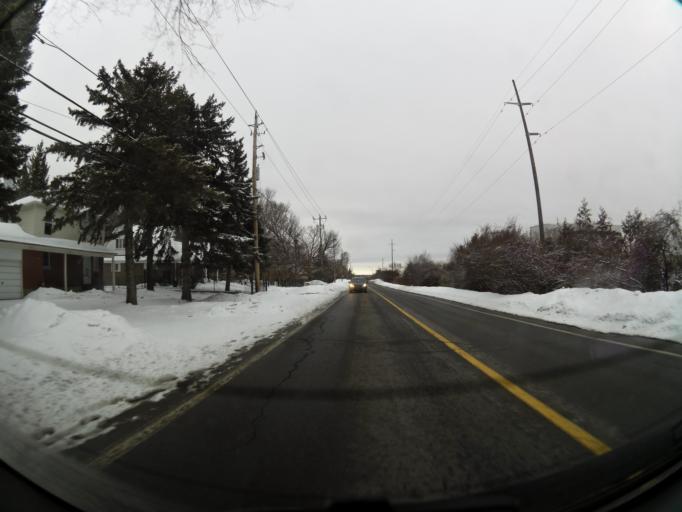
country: CA
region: Quebec
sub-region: Outaouais
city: Gatineau
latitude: 45.4496
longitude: -75.6168
